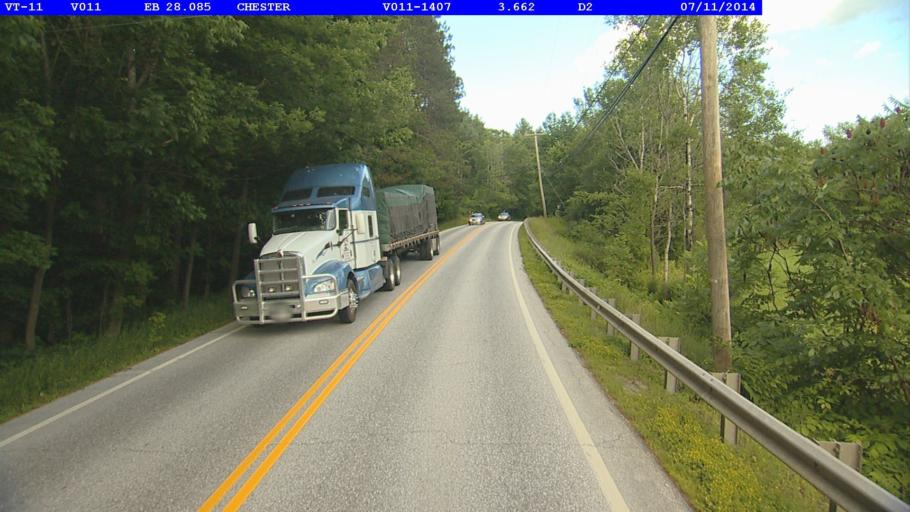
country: US
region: Vermont
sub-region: Windsor County
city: Chester
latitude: 43.2698
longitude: -72.6214
